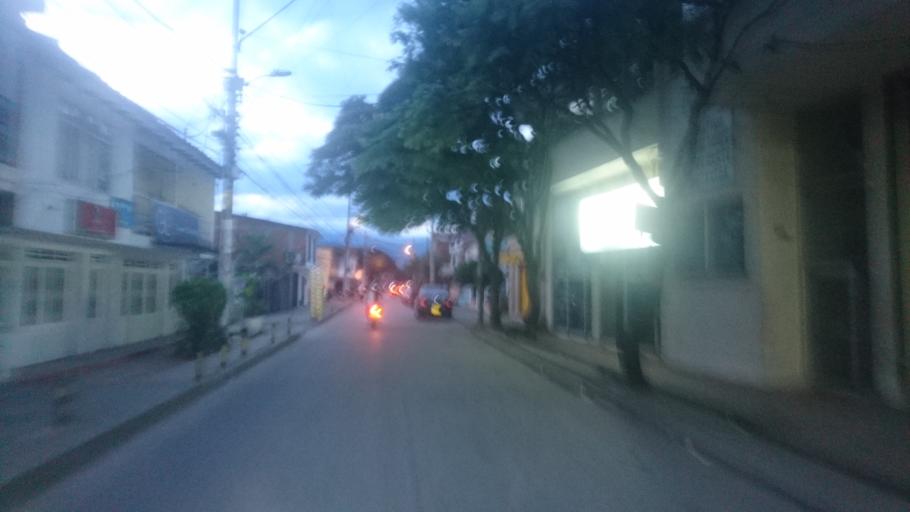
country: CO
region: Valle del Cauca
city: Jamundi
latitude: 3.2637
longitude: -76.5397
